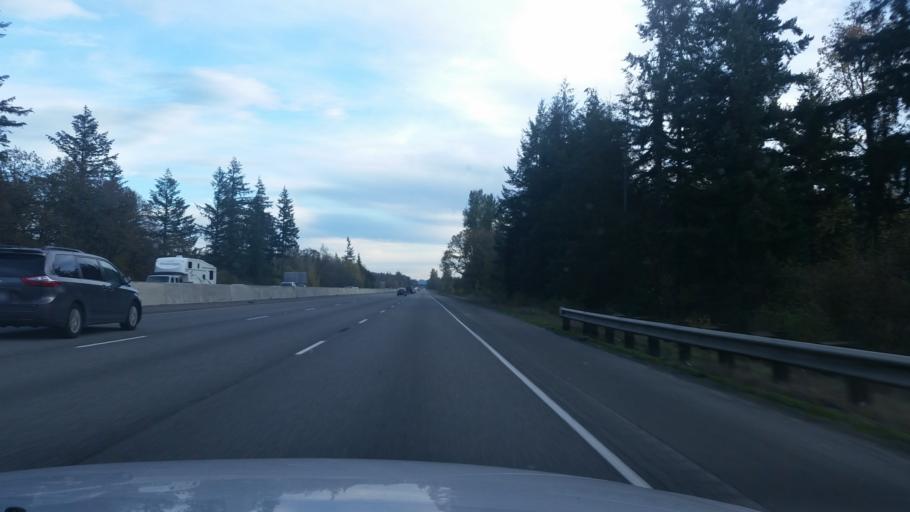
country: US
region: Washington
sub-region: Thurston County
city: Grand Mound
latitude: 46.7908
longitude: -123.0086
